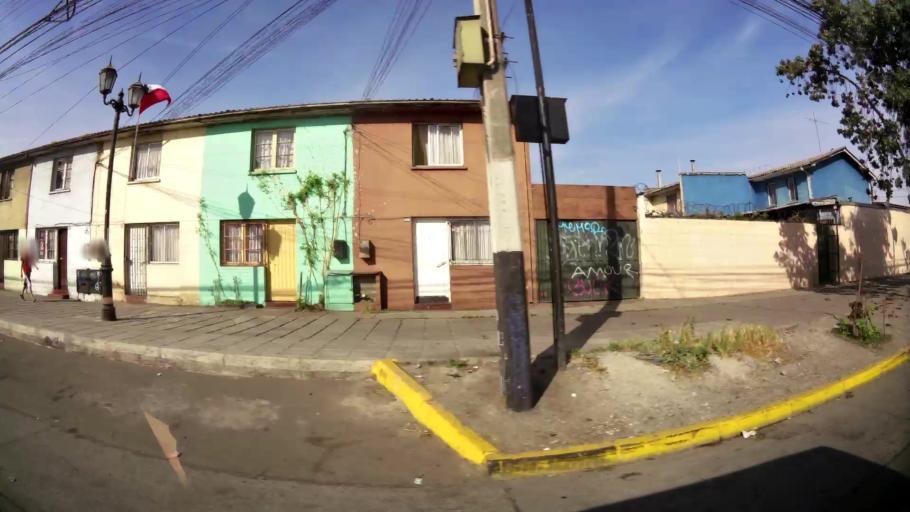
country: CL
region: Santiago Metropolitan
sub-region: Provincia de Santiago
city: La Pintana
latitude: -33.5202
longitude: -70.6364
